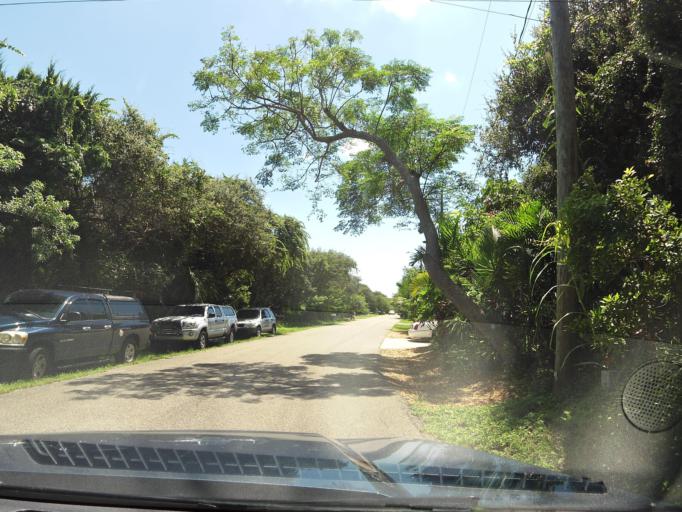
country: US
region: Florida
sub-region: Flagler County
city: Flagler Beach
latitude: 29.4494
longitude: -81.1147
